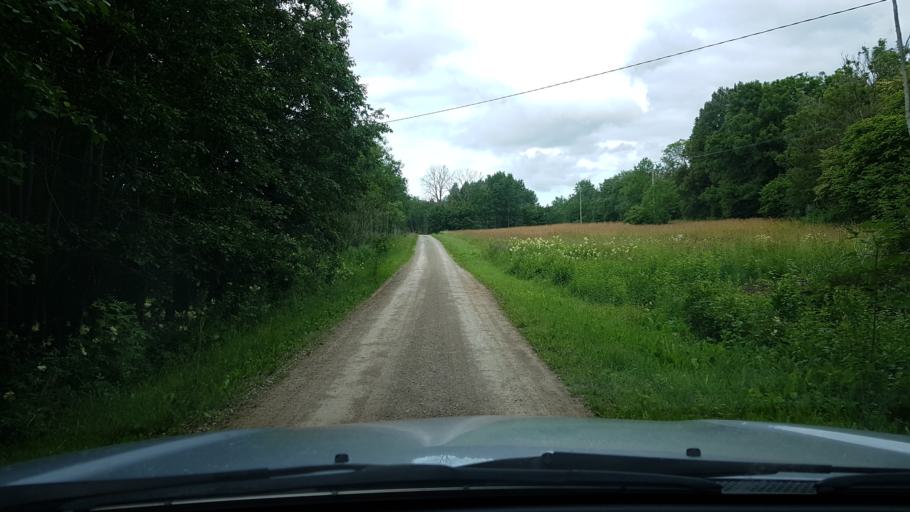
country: EE
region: Ida-Virumaa
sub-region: Narva-Joesuu linn
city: Narva-Joesuu
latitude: 59.4058
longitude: 27.9741
